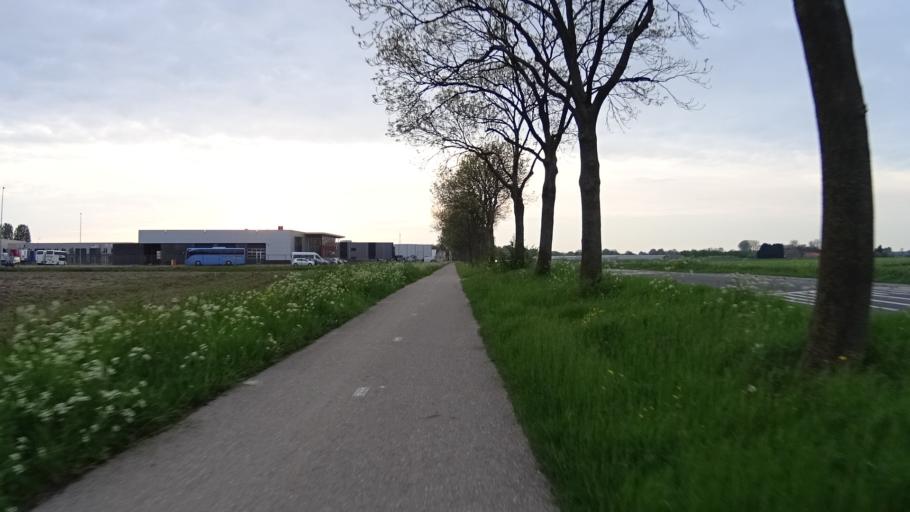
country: NL
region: North Brabant
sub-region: Gemeente Woudrichem
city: Woudrichem
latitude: 51.7806
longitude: 5.0430
